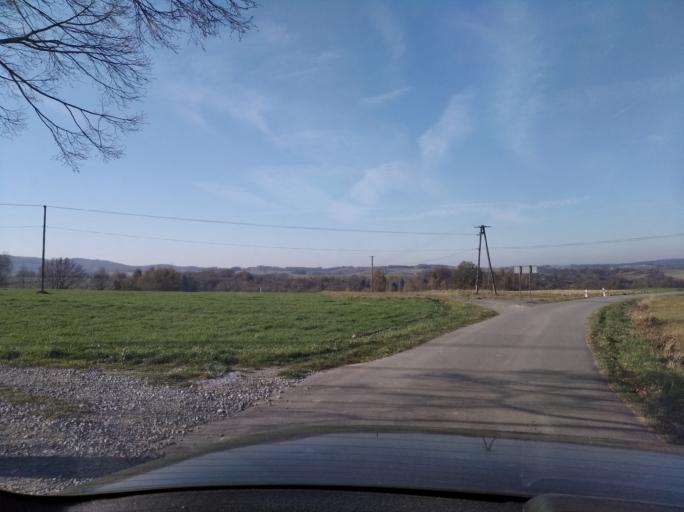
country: PL
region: Subcarpathian Voivodeship
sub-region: Powiat ropczycko-sedziszowski
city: Wielopole Skrzynskie
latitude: 49.9199
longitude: 21.5630
